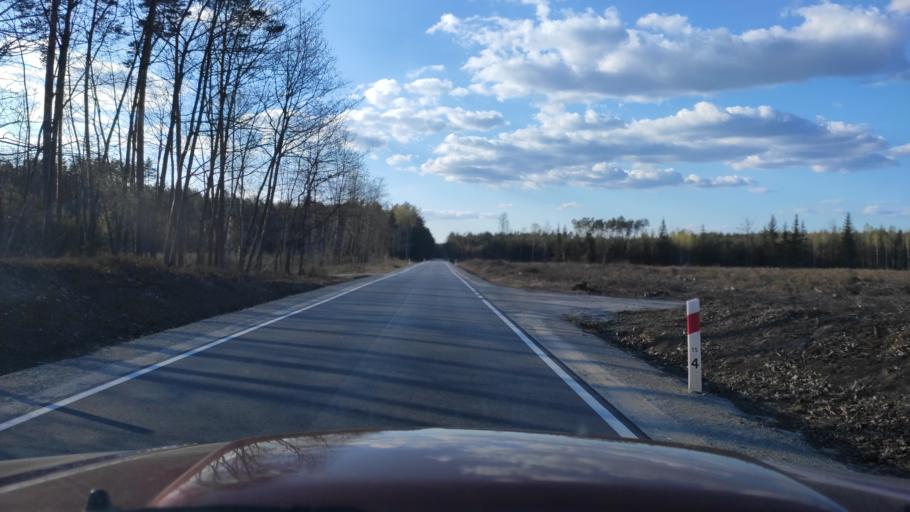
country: PL
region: Masovian Voivodeship
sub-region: Powiat zwolenski
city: Zwolen
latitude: 51.3963
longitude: 21.5427
